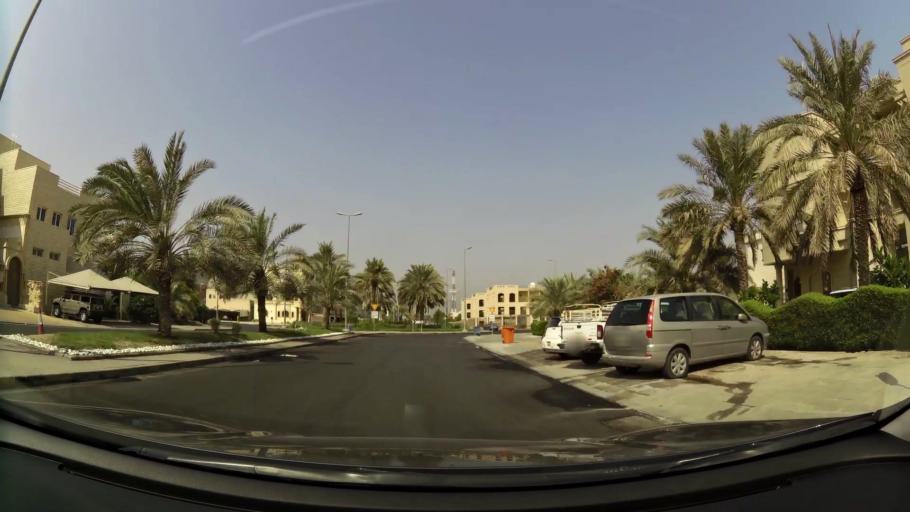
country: KW
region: Al Asimah
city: Ad Dasmah
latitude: 29.3455
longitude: 48.0026
